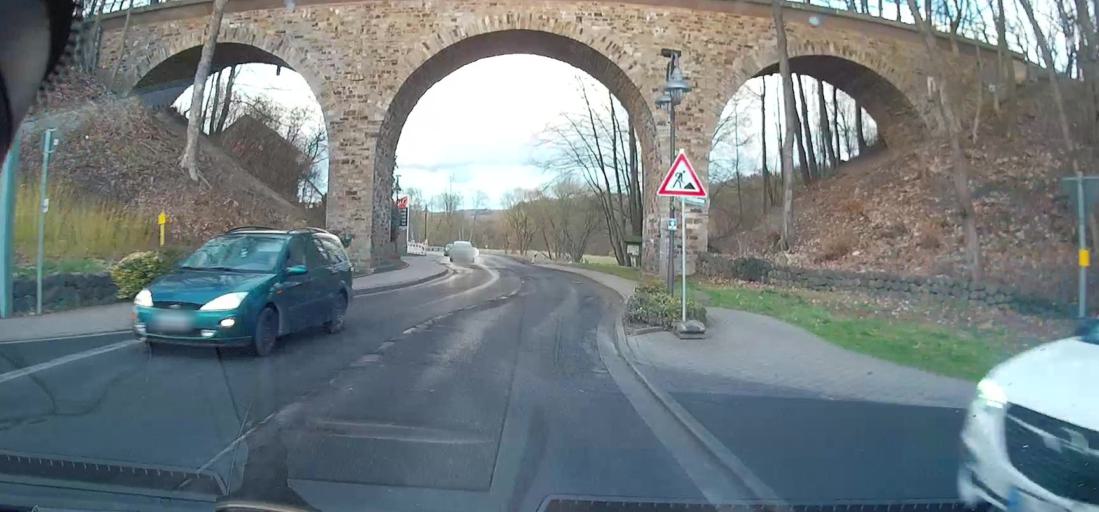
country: DE
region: Rheinland-Pfalz
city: Selters
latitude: 50.5331
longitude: 7.7569
